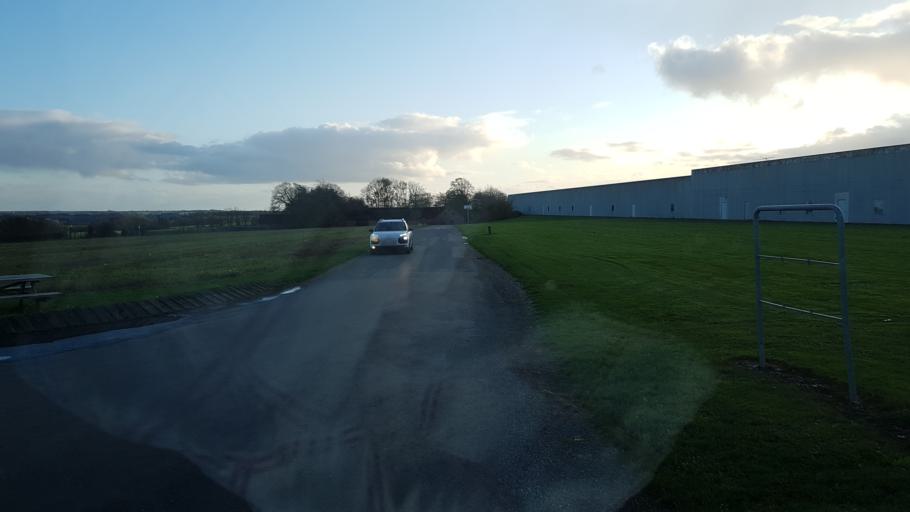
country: DK
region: South Denmark
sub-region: Vejen Kommune
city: Holsted
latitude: 55.4541
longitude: 8.9425
